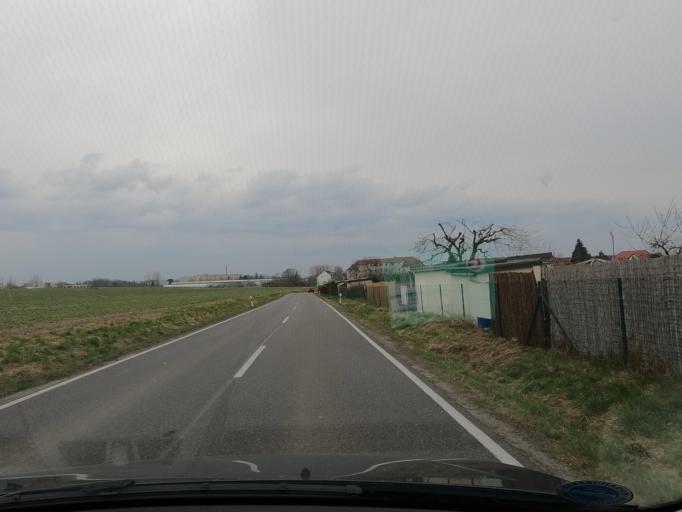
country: DE
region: Saxony
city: Schkeuditz
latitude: 51.4010
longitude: 12.2316
